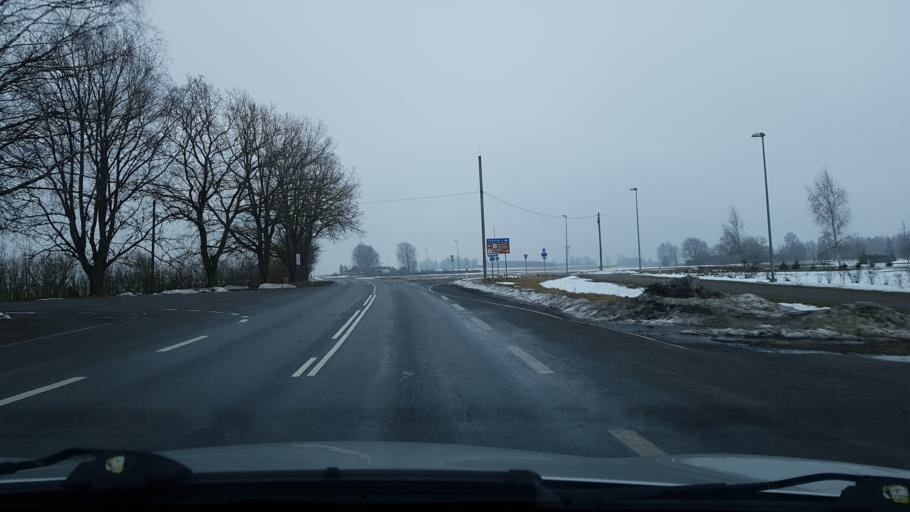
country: EE
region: Valgamaa
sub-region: Torva linn
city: Torva
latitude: 58.2263
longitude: 25.8877
